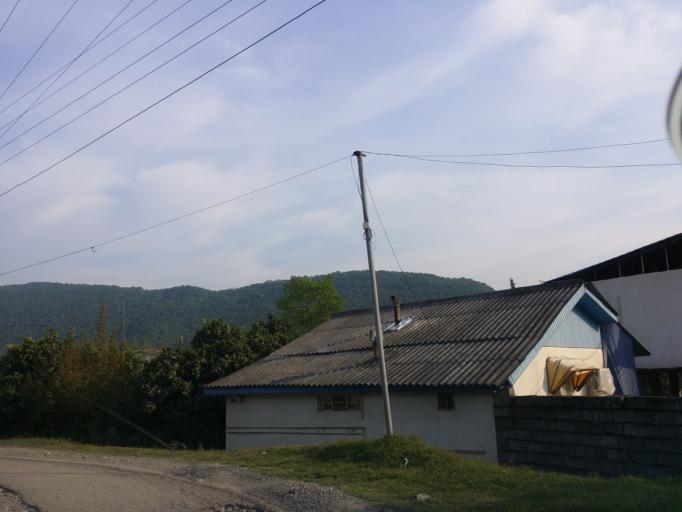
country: IR
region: Mazandaran
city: Chalus
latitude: 36.6552
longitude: 51.3669
